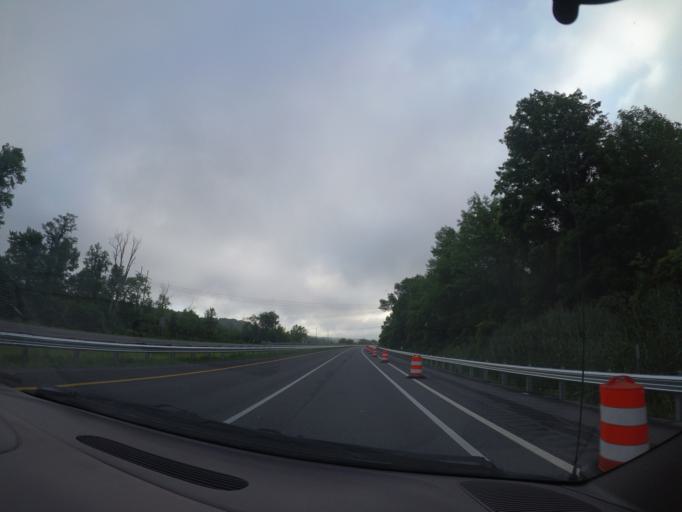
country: US
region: New York
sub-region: Montgomery County
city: Fonda
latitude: 42.9413
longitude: -74.4018
